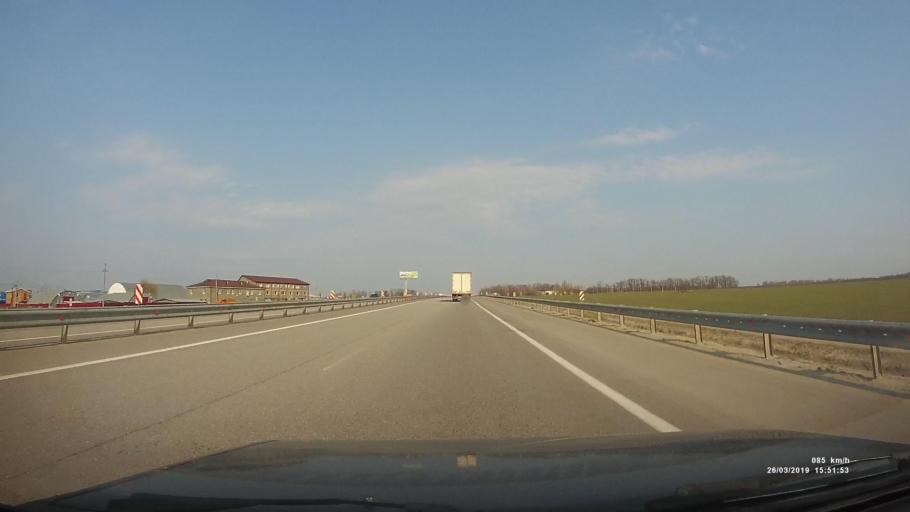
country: RU
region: Rostov
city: Kalinin
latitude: 47.2709
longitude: 39.5128
